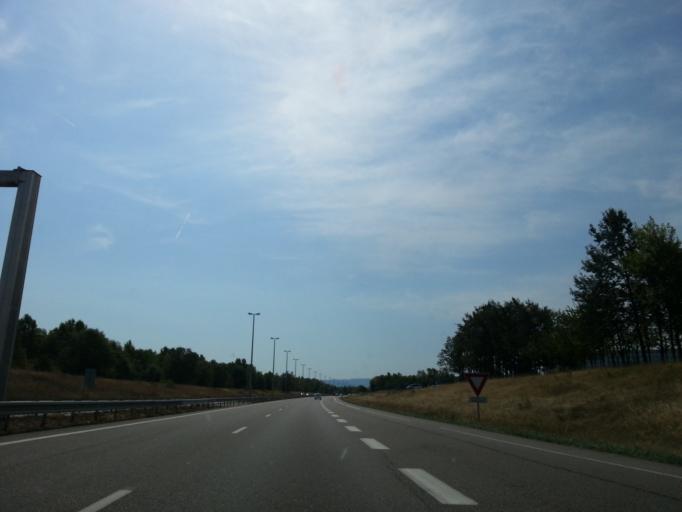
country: FR
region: Alsace
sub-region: Departement du Haut-Rhin
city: Saint-Louis
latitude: 47.5990
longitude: 7.5387
